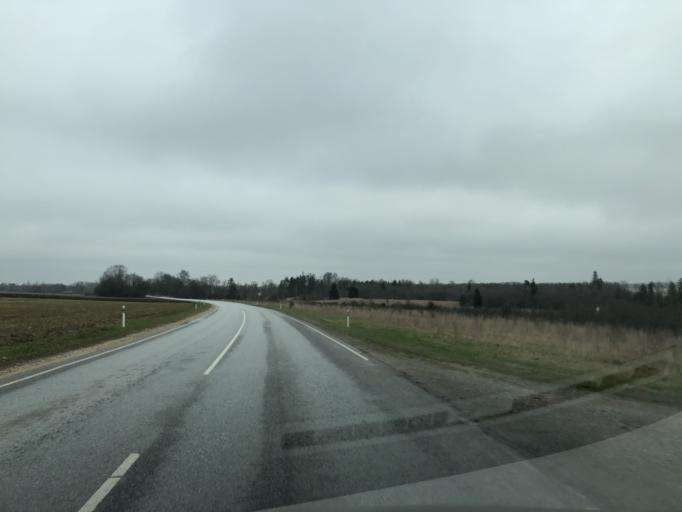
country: EE
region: Laeaene-Virumaa
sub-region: Rakke vald
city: Rakke
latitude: 58.9616
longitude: 26.2789
